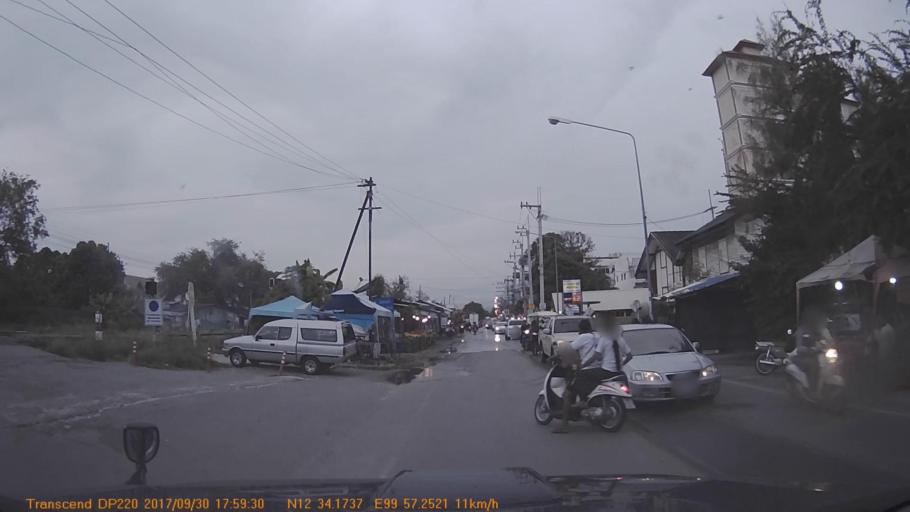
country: TH
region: Prachuap Khiri Khan
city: Hua Hin
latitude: 12.5696
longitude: 99.9542
